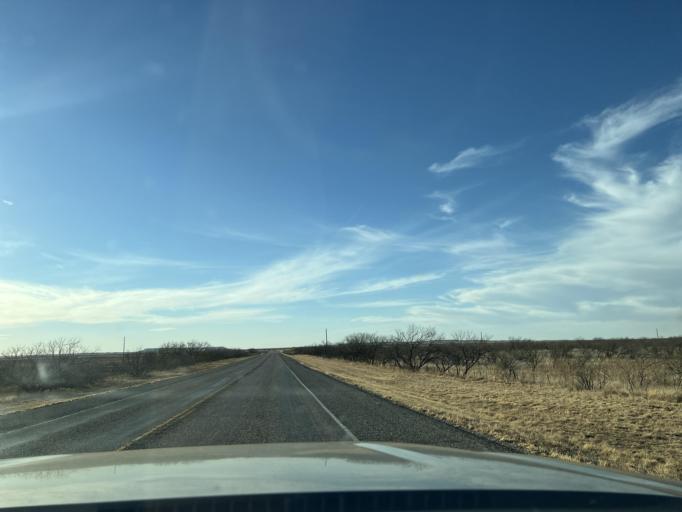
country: US
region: Texas
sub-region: Borden County
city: Gail
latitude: 32.7696
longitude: -101.3225
